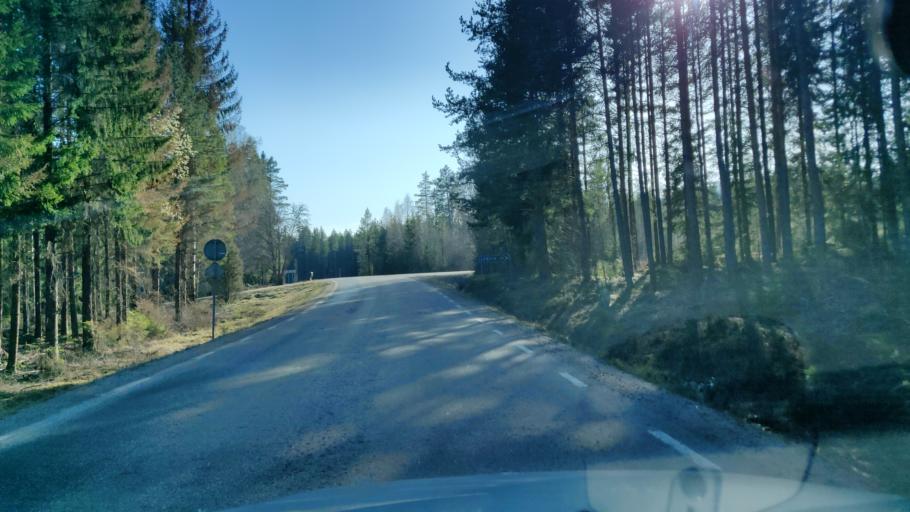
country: SE
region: Vaermland
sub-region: Sunne Kommun
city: Sunne
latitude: 59.9802
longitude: 13.2544
